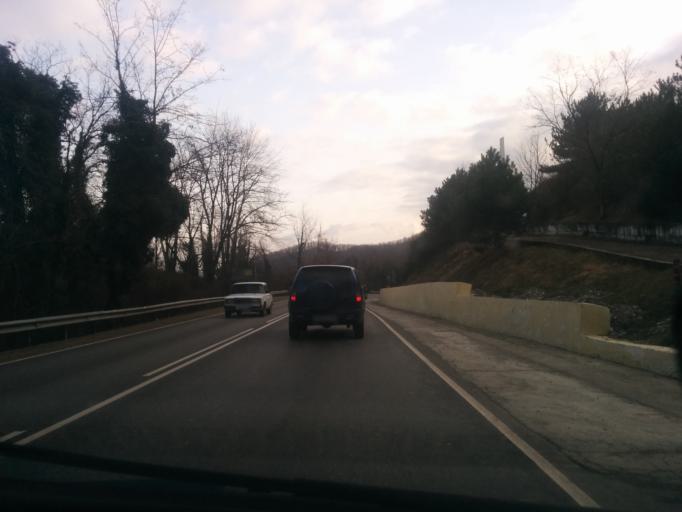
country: RU
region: Krasnodarskiy
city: Agoy
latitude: 44.1267
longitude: 39.0481
